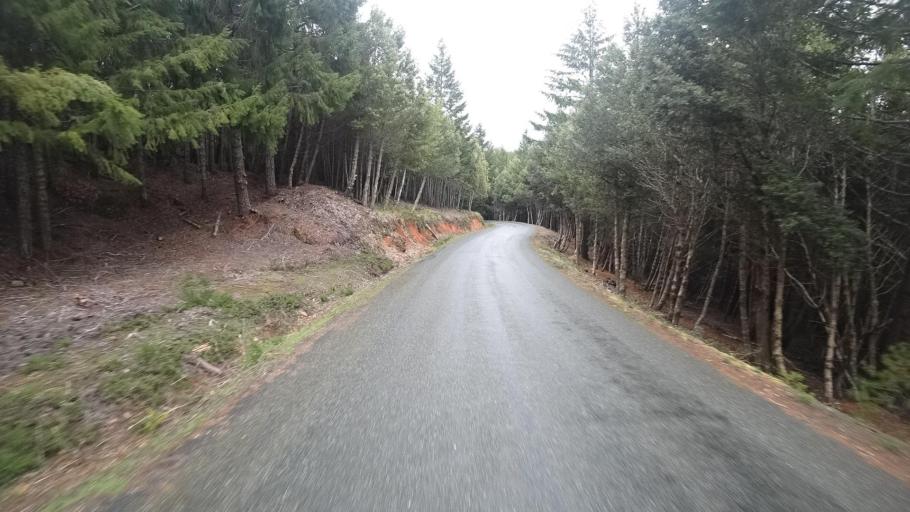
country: US
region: California
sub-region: Humboldt County
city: Willow Creek
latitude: 41.2000
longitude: -123.7934
